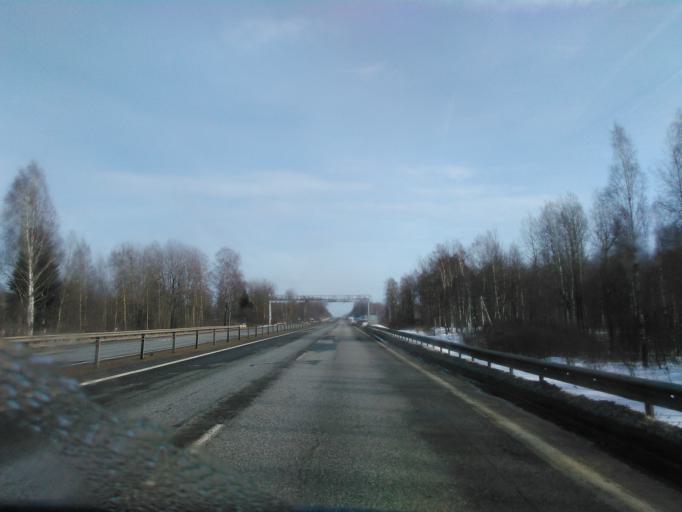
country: BY
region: Vitebsk
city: Dubrowna
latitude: 54.6847
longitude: 30.8070
